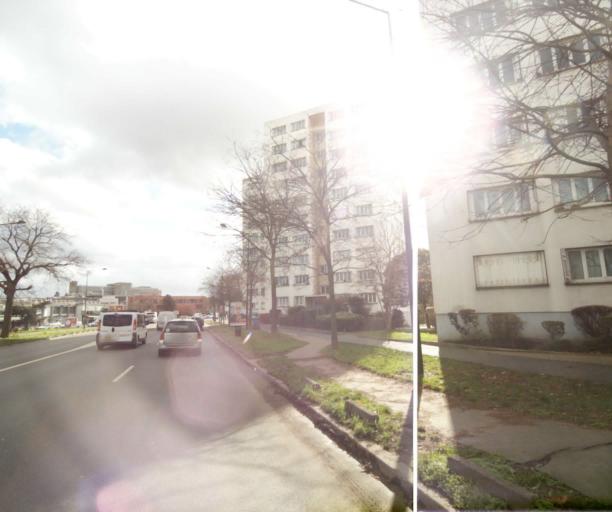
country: FR
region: Ile-de-France
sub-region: Departement de Seine-Saint-Denis
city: Saint-Denis
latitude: 48.9382
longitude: 2.3706
